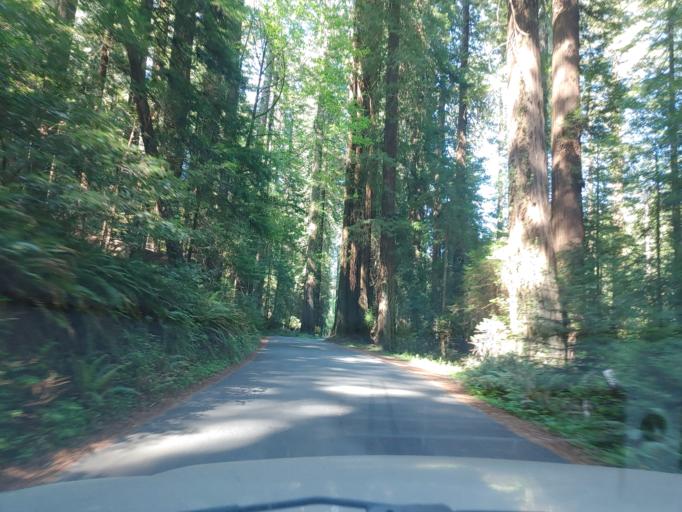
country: US
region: California
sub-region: Humboldt County
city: Rio Dell
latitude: 40.3466
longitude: -123.9331
